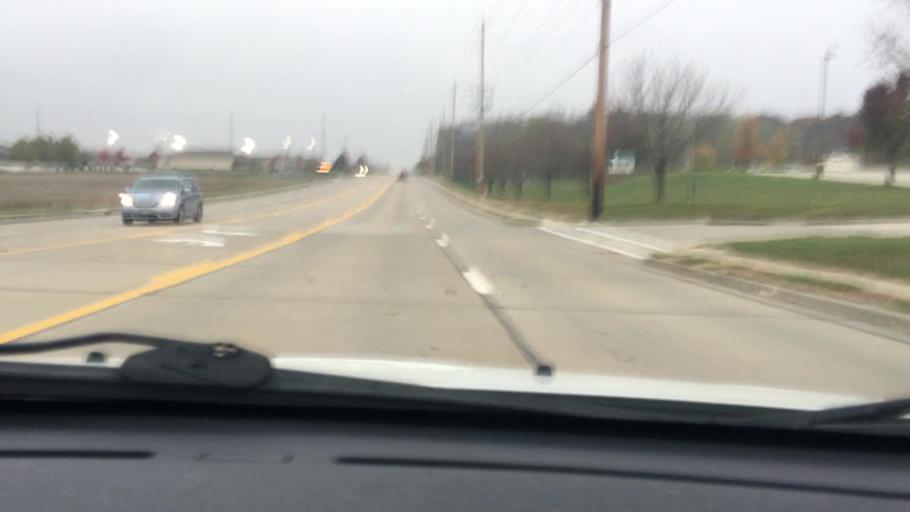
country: US
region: Missouri
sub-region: Saint Charles County
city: O'Fallon
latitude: 38.8215
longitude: -90.6724
